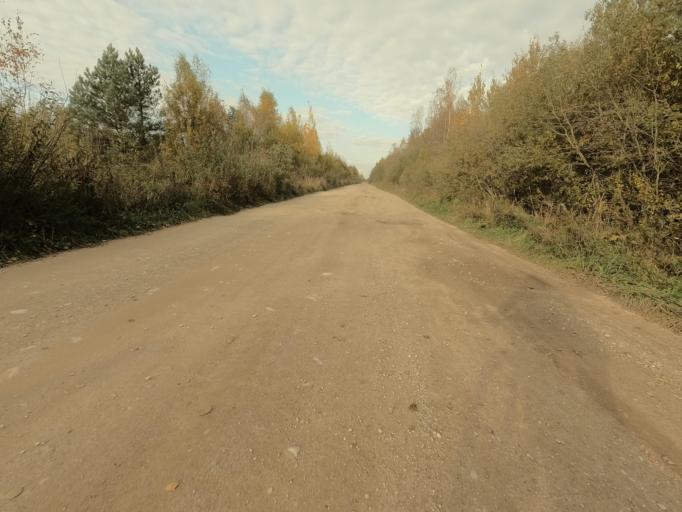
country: RU
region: Novgorod
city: Volkhovskiy
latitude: 58.9084
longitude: 31.0382
